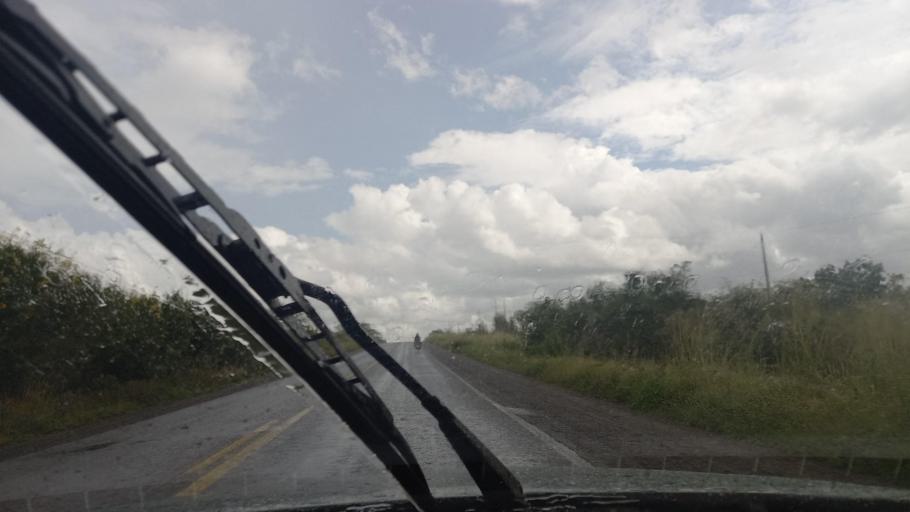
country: BR
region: Pernambuco
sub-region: Cachoeirinha
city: Cachoeirinha
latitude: -8.5674
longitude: -36.2801
